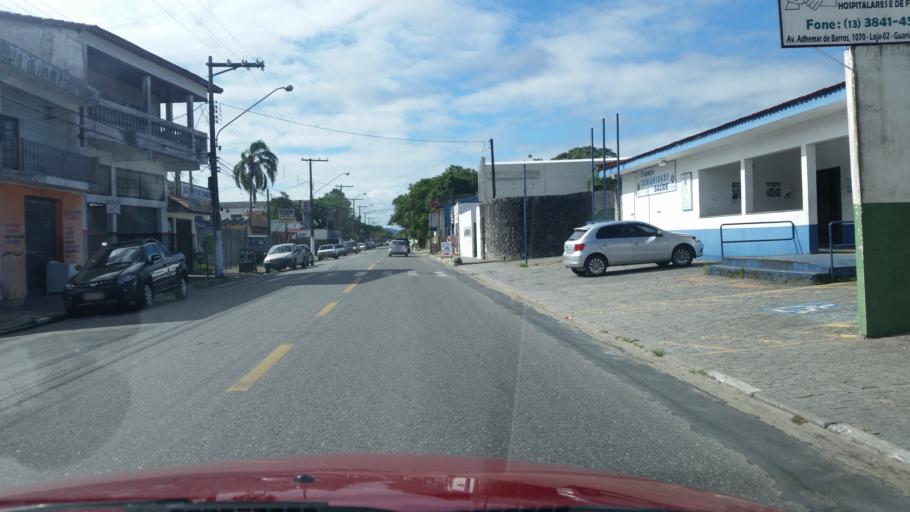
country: BR
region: Sao Paulo
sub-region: Iguape
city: Iguape
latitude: -24.6991
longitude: -47.5633
